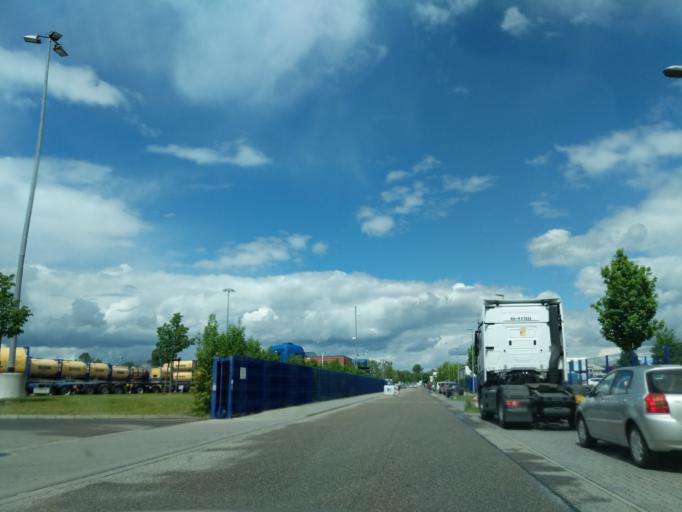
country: DE
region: Rheinland-Pfalz
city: Fussgonheim
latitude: 49.4681
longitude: 8.2910
